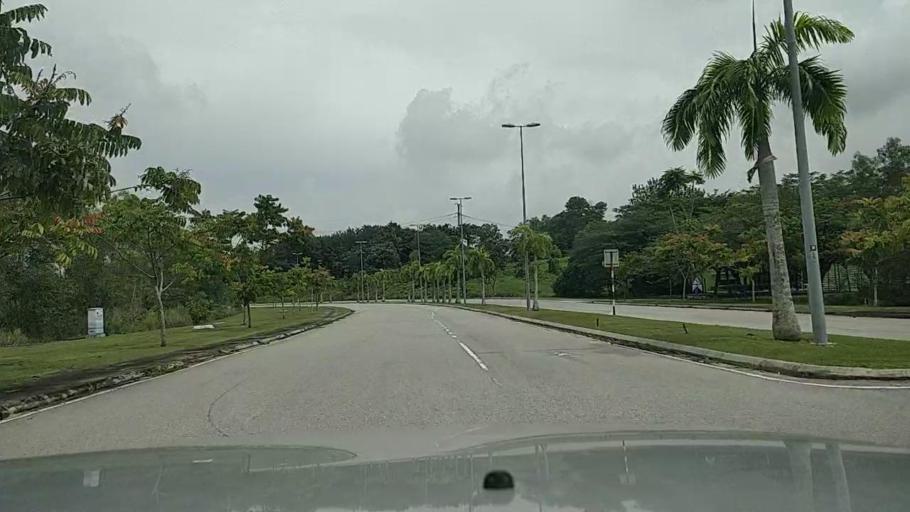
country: MY
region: Putrajaya
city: Putrajaya
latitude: 2.9016
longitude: 101.6506
